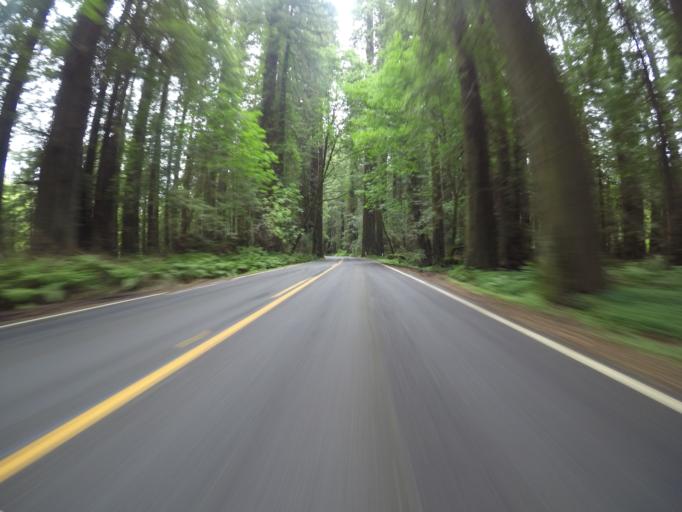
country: US
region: California
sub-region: Humboldt County
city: Rio Dell
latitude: 40.4437
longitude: -124.0208
